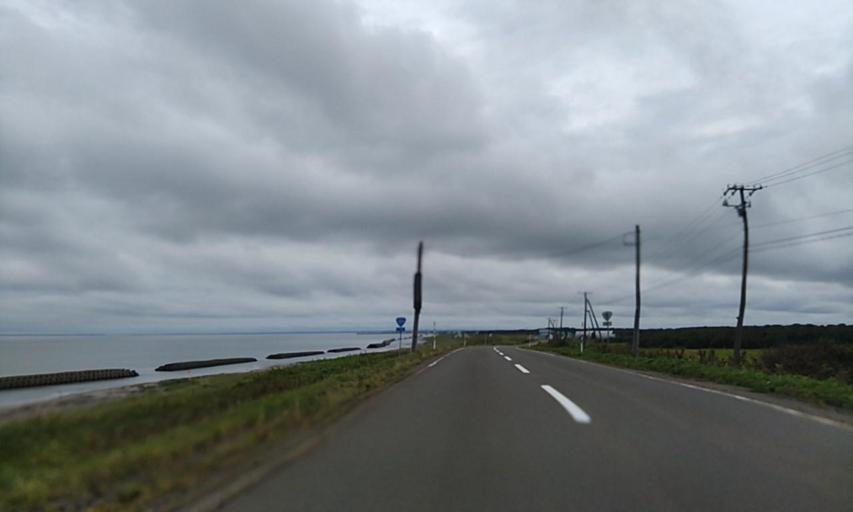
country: JP
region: Hokkaido
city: Shibetsu
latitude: 43.4210
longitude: 145.2682
